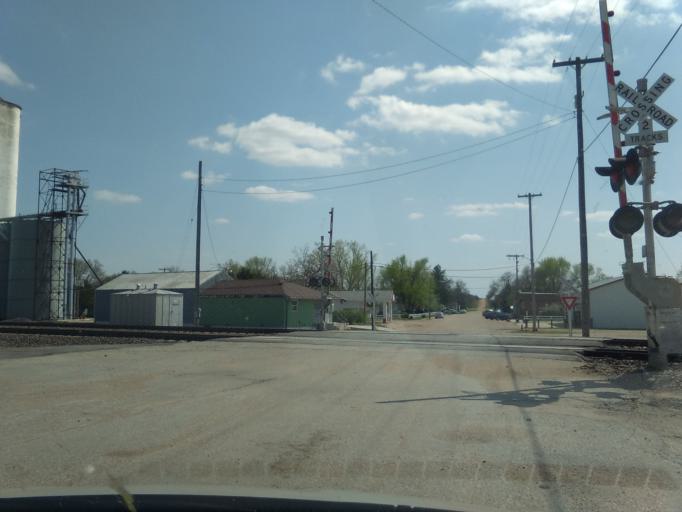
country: US
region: Nebraska
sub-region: Thayer County
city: Hebron
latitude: 40.2531
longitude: -97.5580
